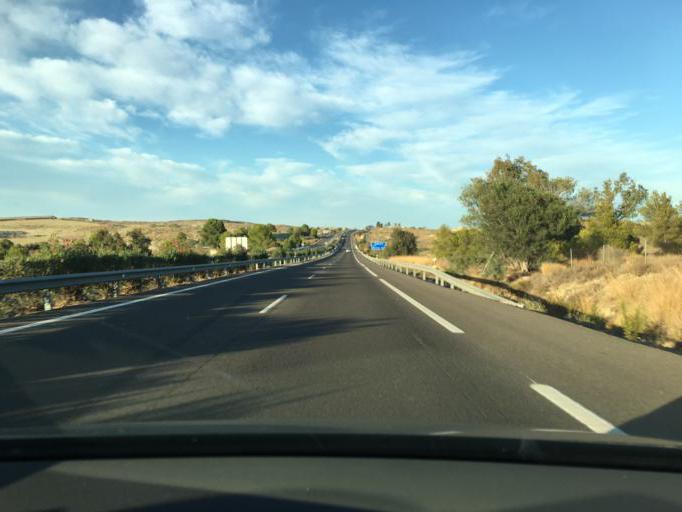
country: ES
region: Andalusia
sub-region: Provincia de Almeria
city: Turre
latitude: 37.1972
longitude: -1.9113
